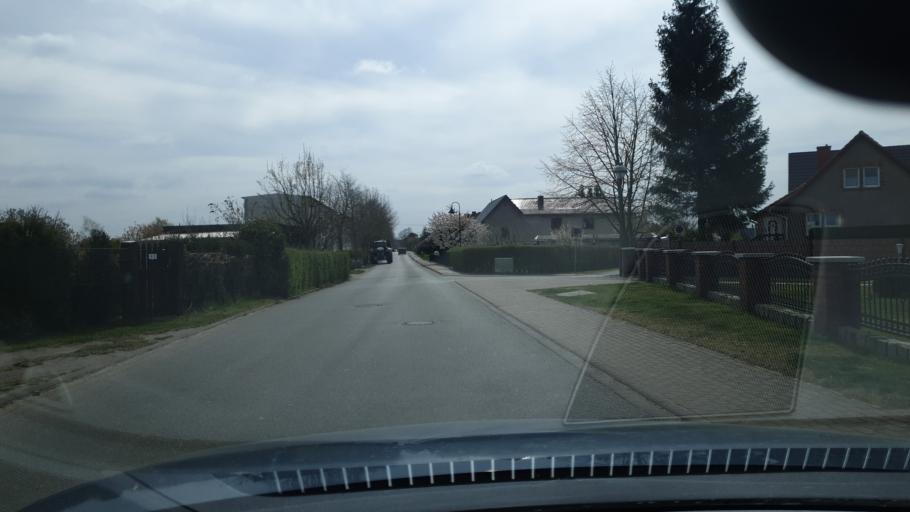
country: DE
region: Mecklenburg-Vorpommern
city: Wittenforden
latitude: 53.6321
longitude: 11.3189
